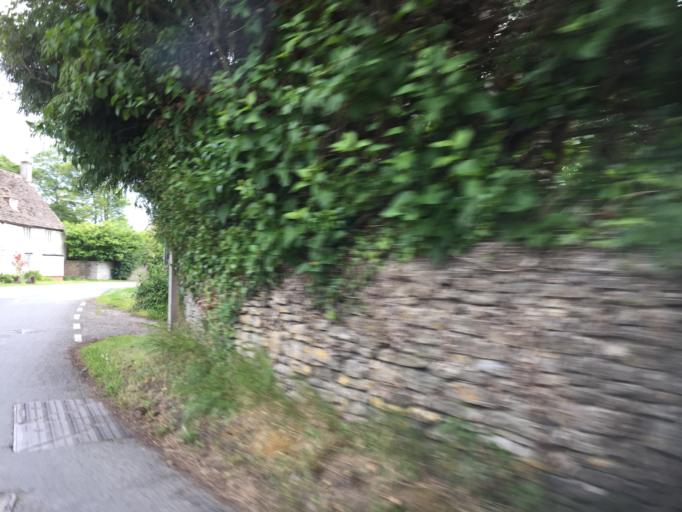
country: GB
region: England
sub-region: Wiltshire
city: Minety
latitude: 51.6470
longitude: -1.9361
